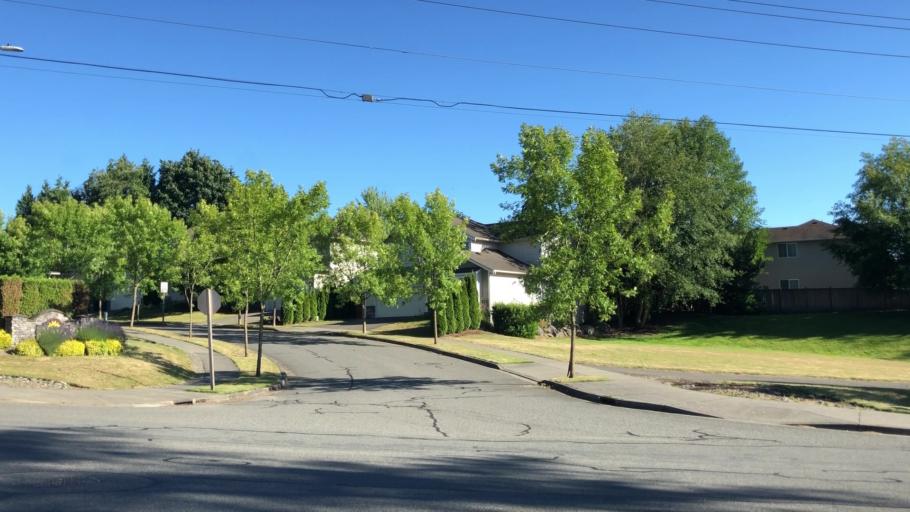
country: US
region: Washington
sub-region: Snohomish County
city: Martha Lake
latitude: 47.8362
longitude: -122.2574
